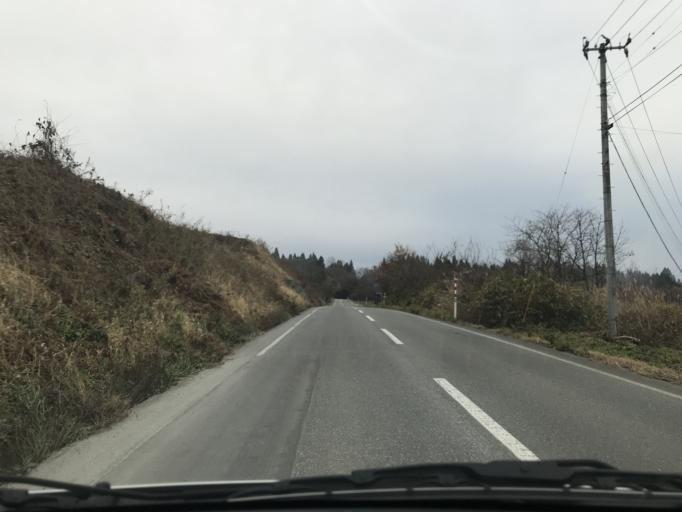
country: JP
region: Iwate
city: Kitakami
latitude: 39.2546
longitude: 141.2677
